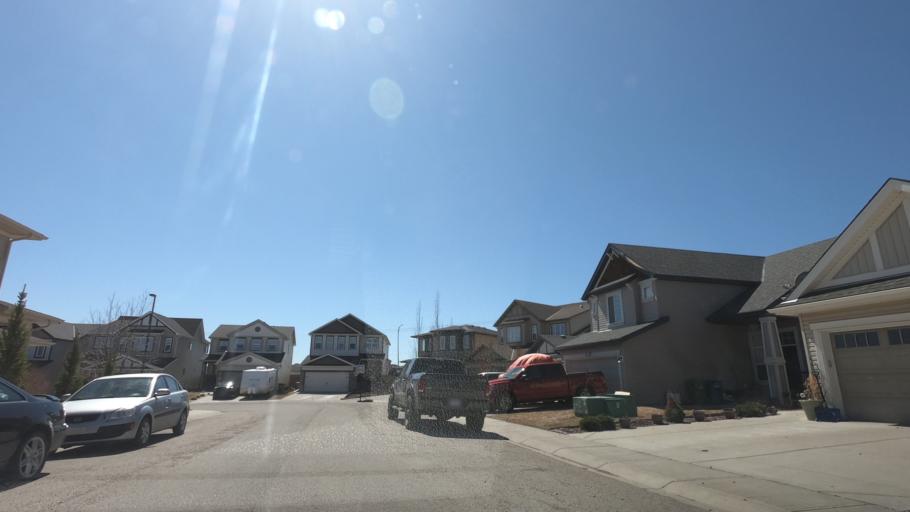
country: CA
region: Alberta
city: Airdrie
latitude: 51.3010
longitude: -114.0477
